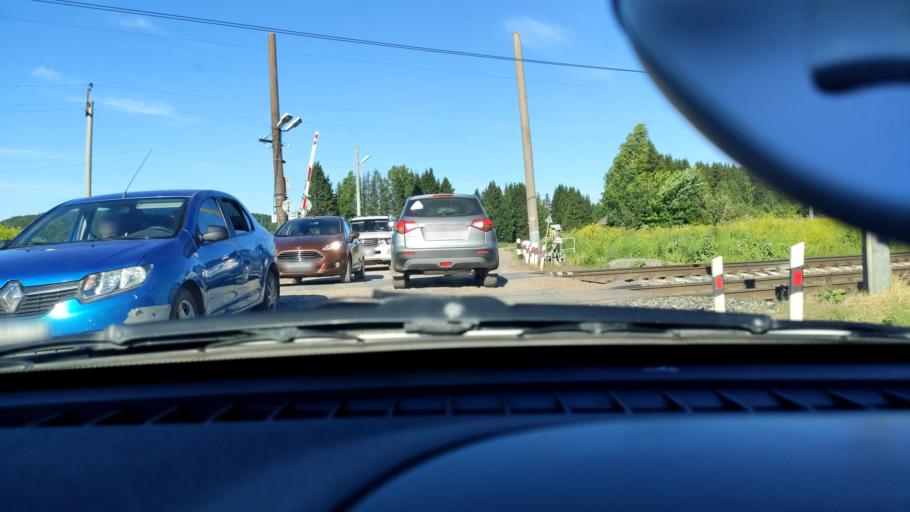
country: RU
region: Perm
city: Bershet'
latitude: 57.6927
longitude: 56.4025
